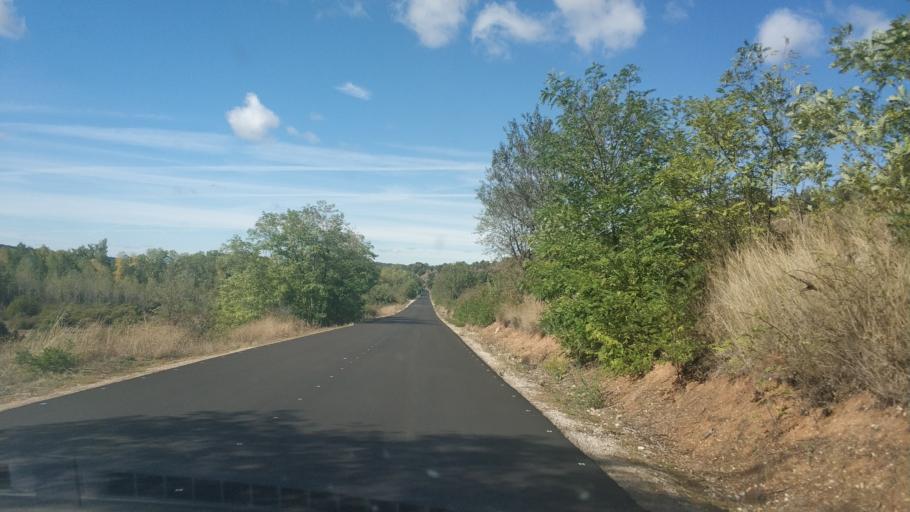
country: ES
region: Castille and Leon
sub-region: Provincia de Burgos
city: Covarrubias
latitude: 42.0482
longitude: -3.5325
